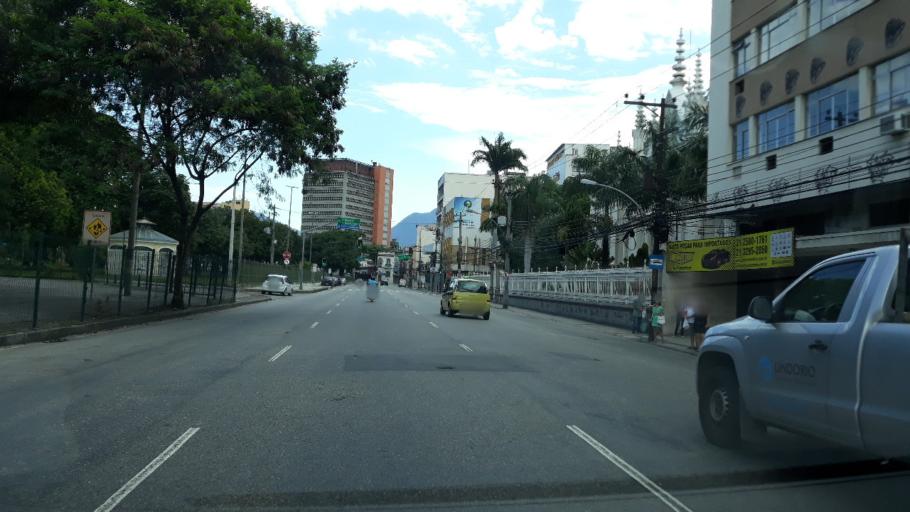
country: BR
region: Rio de Janeiro
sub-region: Rio De Janeiro
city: Rio de Janeiro
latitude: -22.8970
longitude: -43.2218
